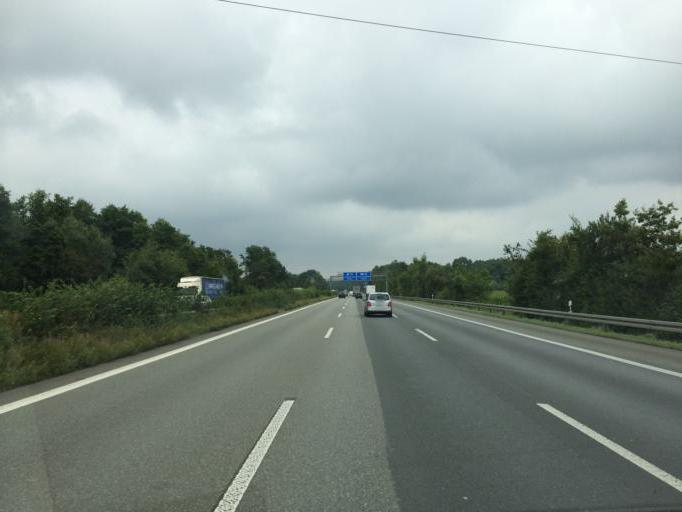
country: DE
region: North Rhine-Westphalia
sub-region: Regierungsbezirk Detmold
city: Verl
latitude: 51.9195
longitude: 8.5215
